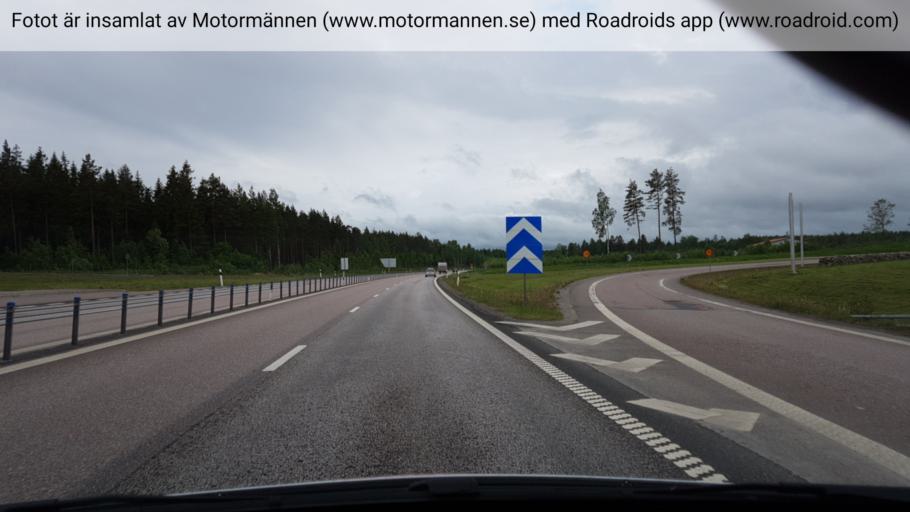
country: SE
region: Vaestra Goetaland
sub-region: Skovde Kommun
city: Skultorp
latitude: 58.3406
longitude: 13.8641
